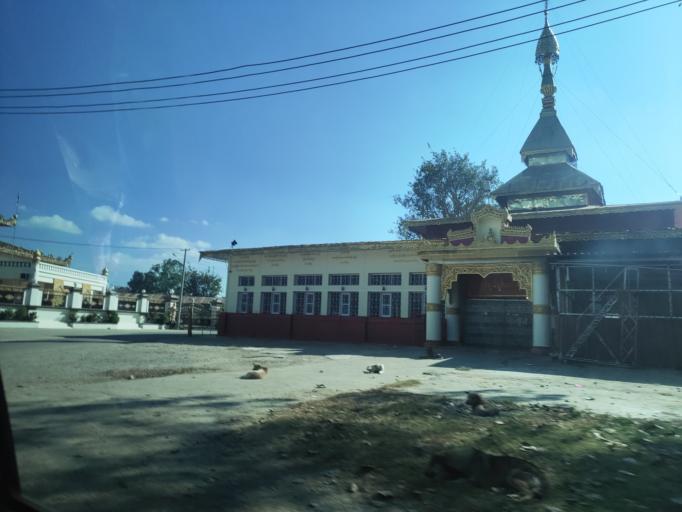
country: MM
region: Mandalay
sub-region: Pyin Oo Lwin District
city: Pyin Oo Lwin
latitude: 22.0363
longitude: 96.4815
